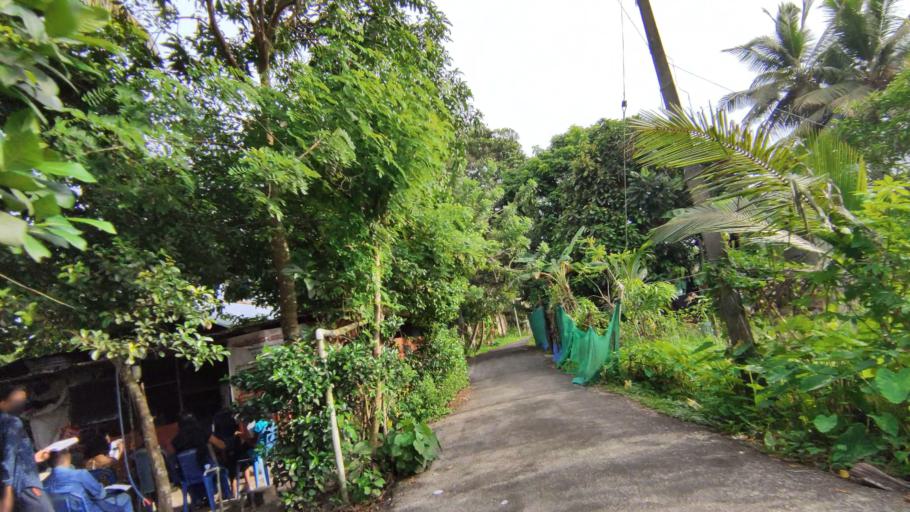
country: IN
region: Kerala
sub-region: Alappuzha
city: Shertallai
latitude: 9.6224
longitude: 76.3378
